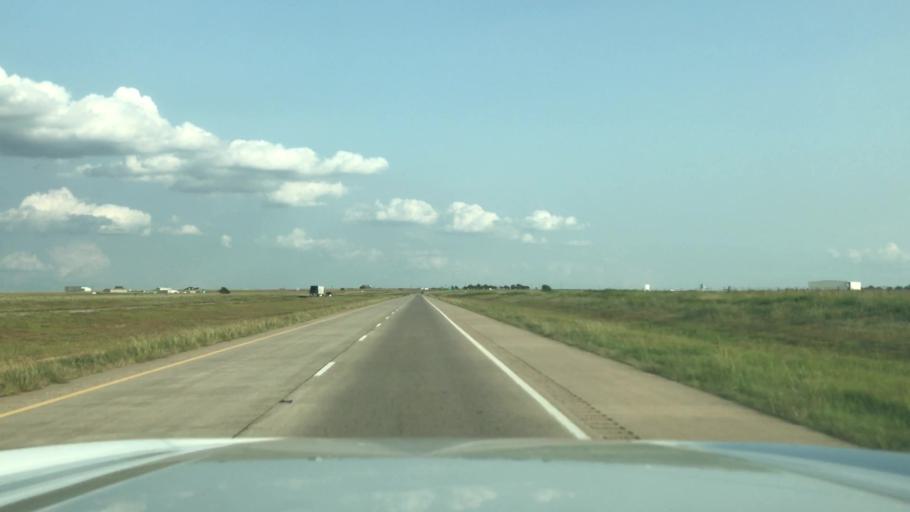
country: US
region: Texas
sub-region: Randall County
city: Canyon
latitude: 34.9542
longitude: -101.8574
